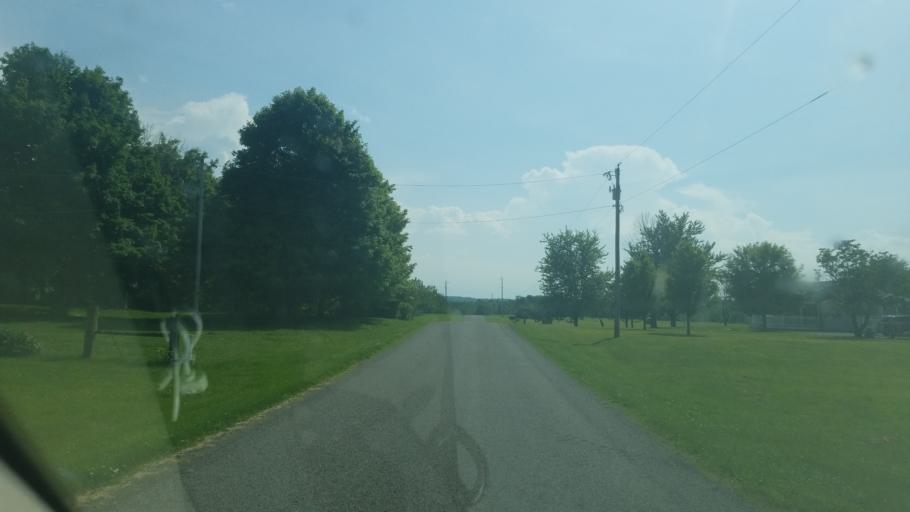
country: US
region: Ohio
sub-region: Champaign County
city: North Lewisburg
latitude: 40.2842
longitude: -83.6361
